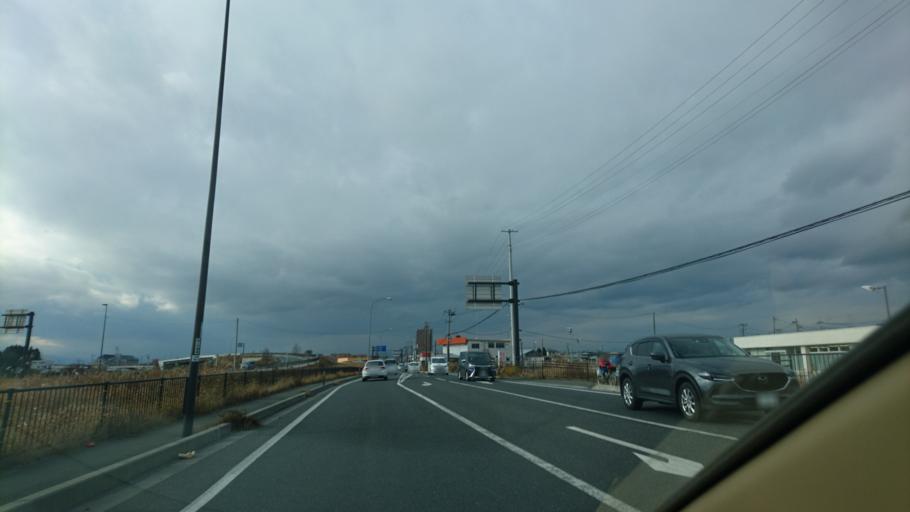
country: JP
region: Miyagi
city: Furukawa
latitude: 38.5687
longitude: 140.9908
